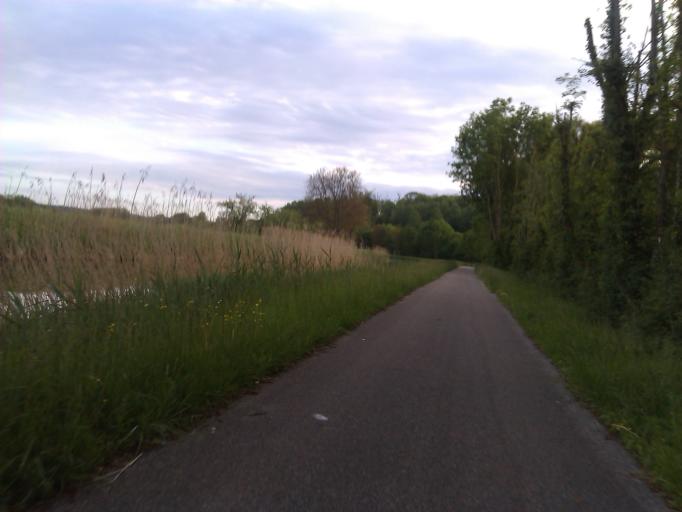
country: FR
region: Franche-Comte
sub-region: Departement du Jura
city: Dole
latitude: 47.1148
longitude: 5.5501
